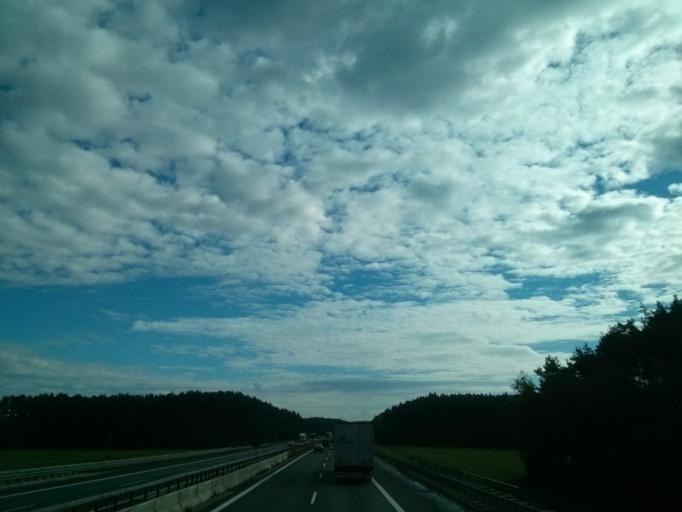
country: DE
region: Bavaria
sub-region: Regierungsbezirk Mittelfranken
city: Rohr
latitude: 49.3159
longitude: 10.8592
